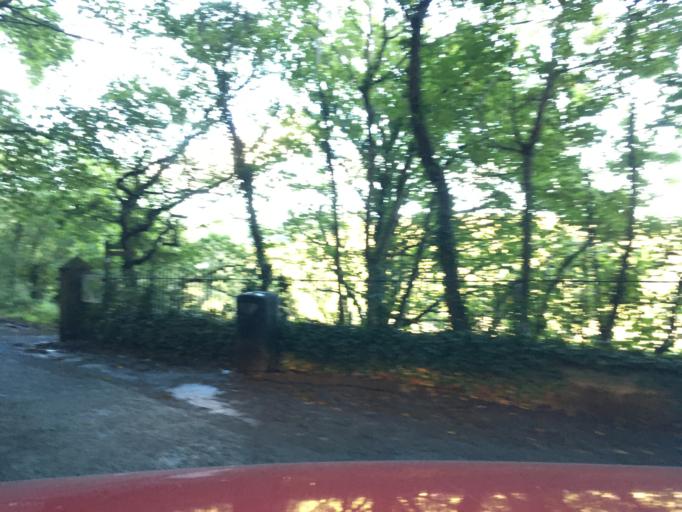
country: GB
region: England
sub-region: Devon
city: Dartmouth
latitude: 50.3413
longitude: -3.5668
